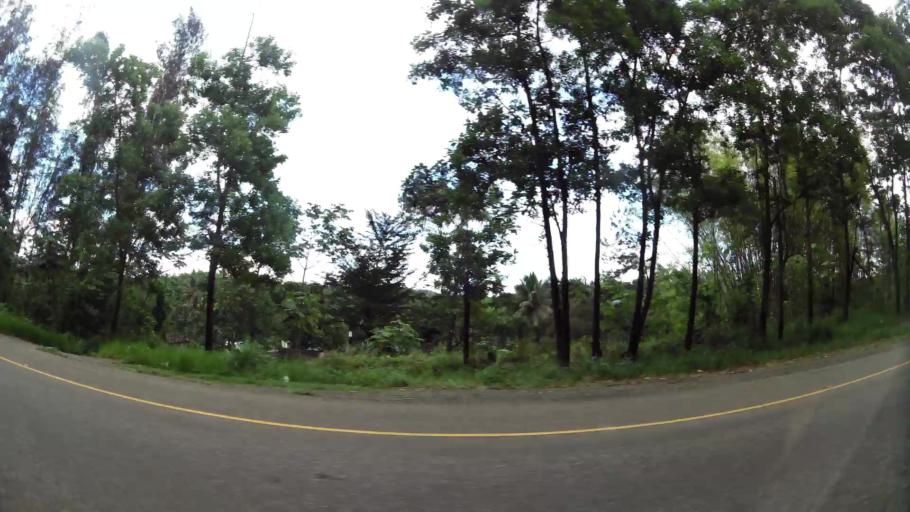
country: DO
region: La Vega
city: Rincon
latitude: 19.1031
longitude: -70.4423
